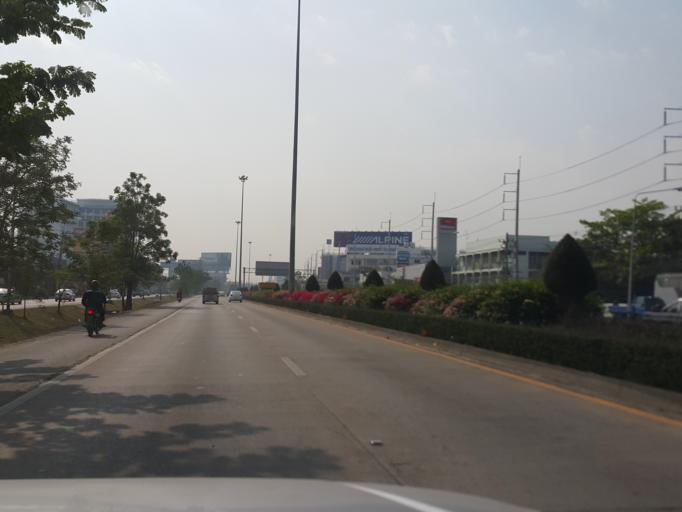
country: TH
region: Chiang Mai
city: Chiang Mai
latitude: 18.7921
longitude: 99.0241
